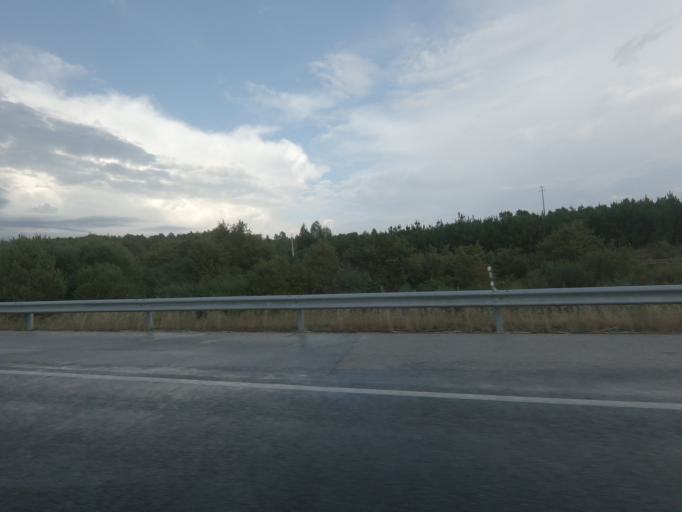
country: PT
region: Viseu
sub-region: Castro Daire
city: Castro Daire
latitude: 40.9347
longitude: -7.9096
